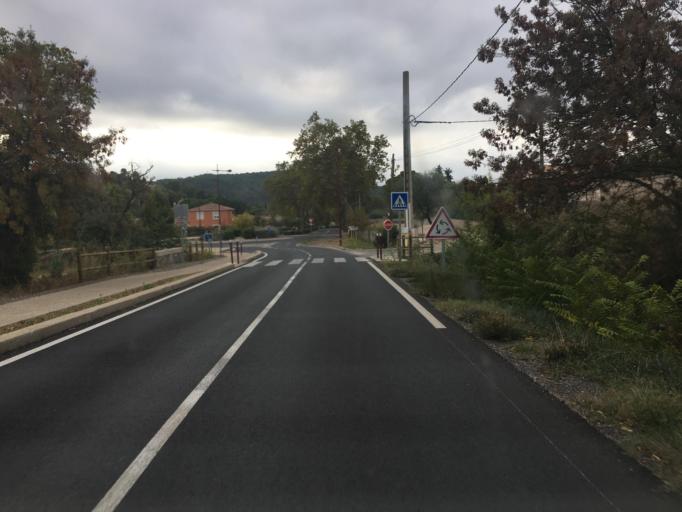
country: FR
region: Languedoc-Roussillon
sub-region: Departement de l'Herault
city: Nebian
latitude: 43.6365
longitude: 3.4184
